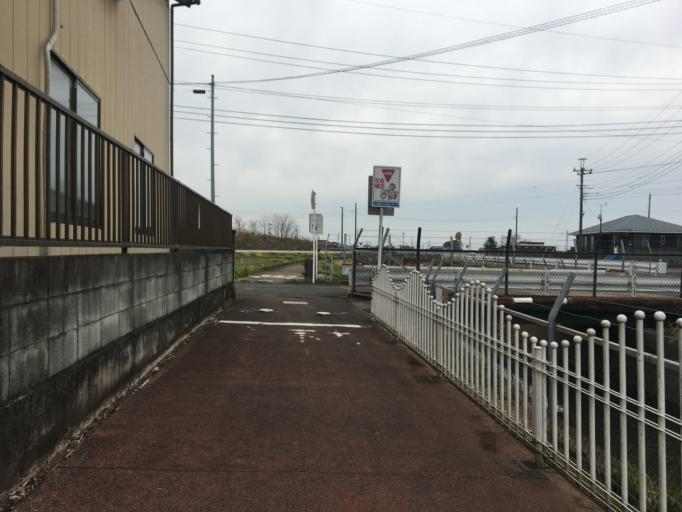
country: JP
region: Saitama
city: Kisai
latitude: 36.1134
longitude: 139.5464
